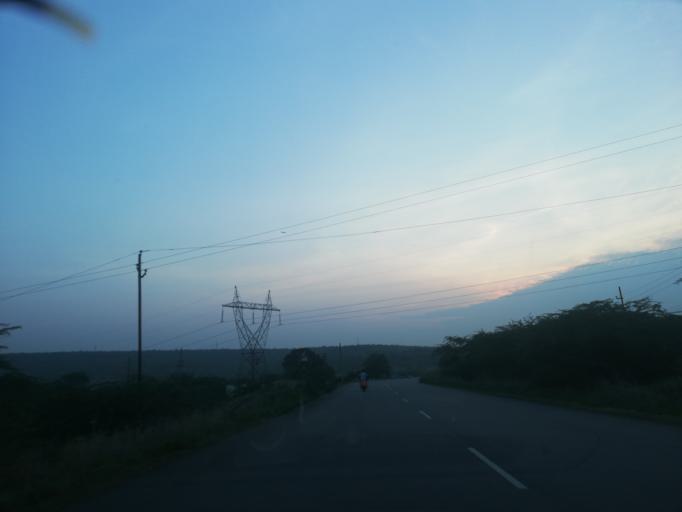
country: IN
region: Andhra Pradesh
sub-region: Guntur
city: Macherla
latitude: 16.5955
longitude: 79.3120
